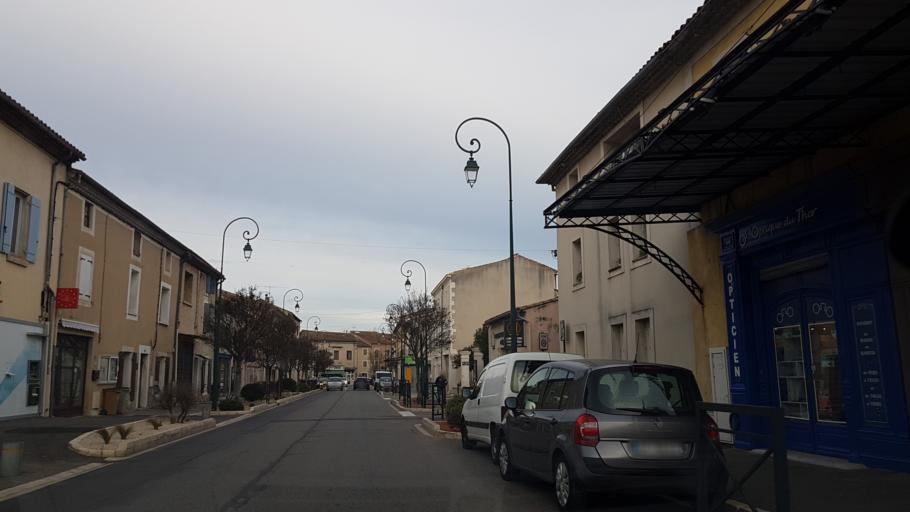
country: FR
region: Provence-Alpes-Cote d'Azur
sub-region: Departement du Vaucluse
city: Le Thor
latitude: 43.9279
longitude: 4.9941
